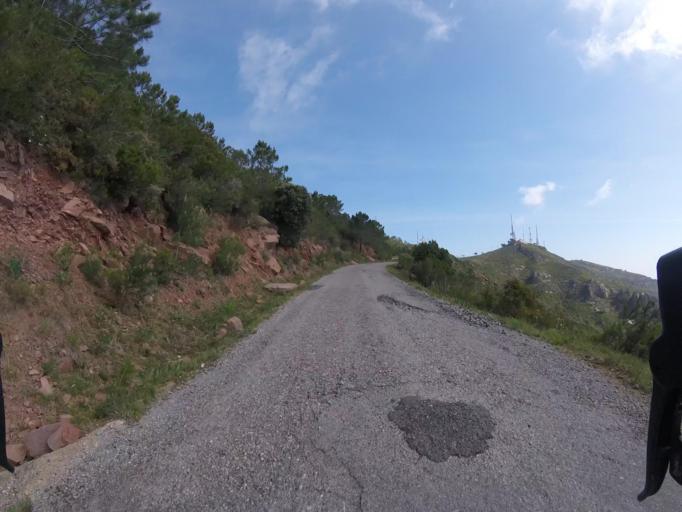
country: ES
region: Valencia
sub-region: Provincia de Castello
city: Benicassim
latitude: 40.0815
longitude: 0.0247
